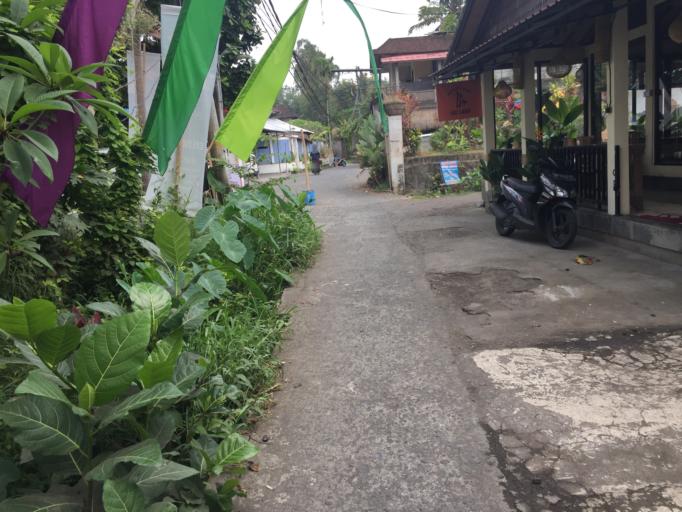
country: ID
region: Bali
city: Banjar Pande
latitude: -8.5065
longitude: 115.2512
